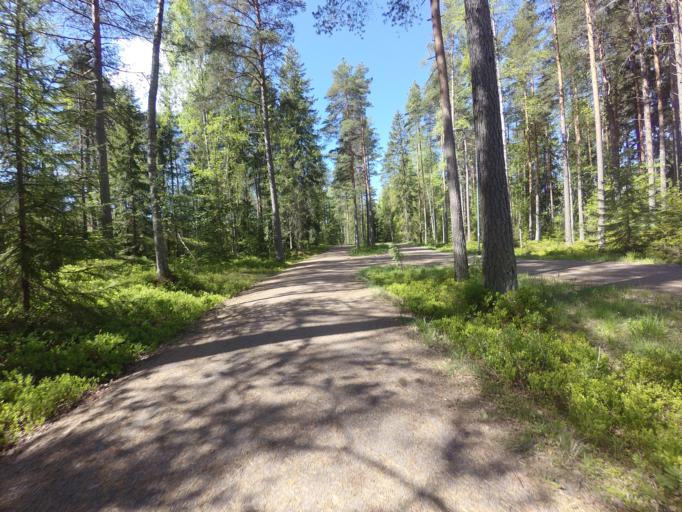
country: FI
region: Uusimaa
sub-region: Helsinki
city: Kauniainen
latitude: 60.1845
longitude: 24.7222
